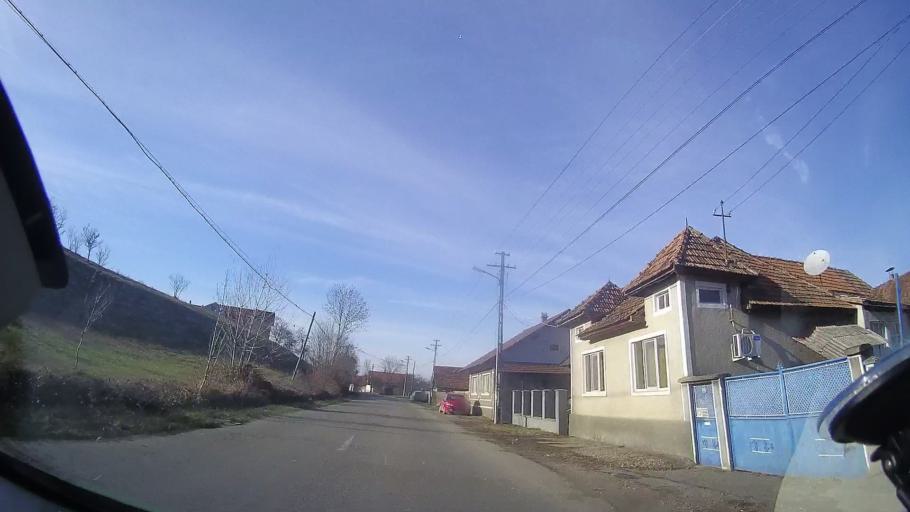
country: RO
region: Bihor
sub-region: Comuna Astileu
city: Astileu
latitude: 47.0278
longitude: 22.3967
